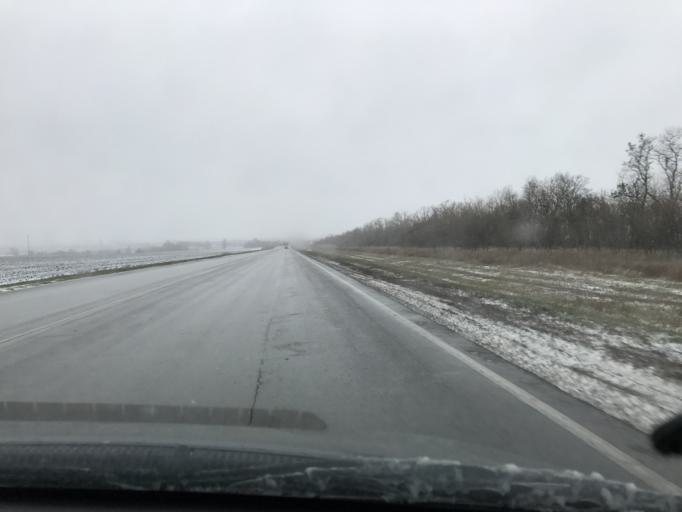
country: RU
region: Rostov
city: Mechetinskaya
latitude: 46.6794
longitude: 40.5237
